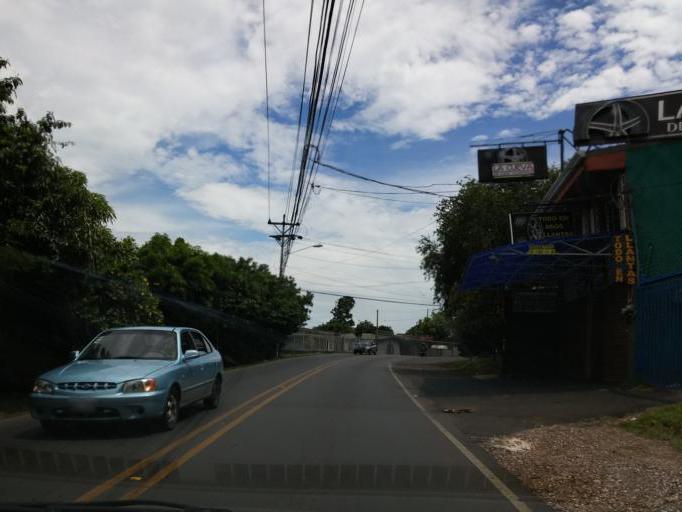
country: CR
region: Alajuela
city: Alajuela
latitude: 10.0125
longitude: -84.2340
